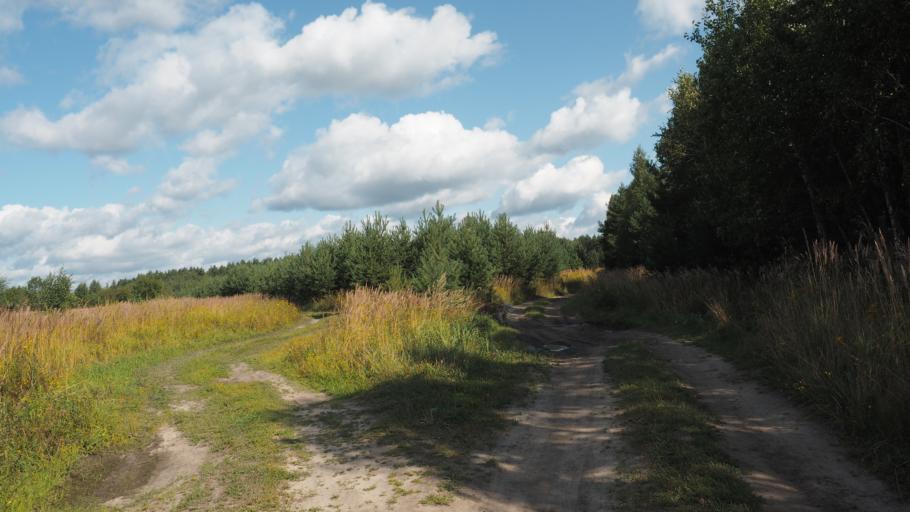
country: RU
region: Moskovskaya
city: Ramenskoye
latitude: 55.5915
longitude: 38.2897
